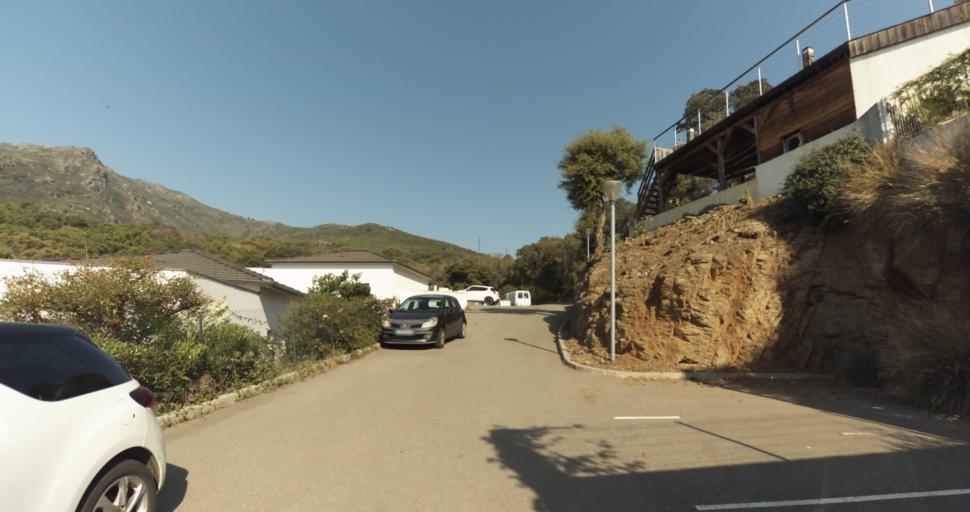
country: FR
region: Corsica
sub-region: Departement de la Haute-Corse
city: Biguglia
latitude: 42.6349
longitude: 9.4257
